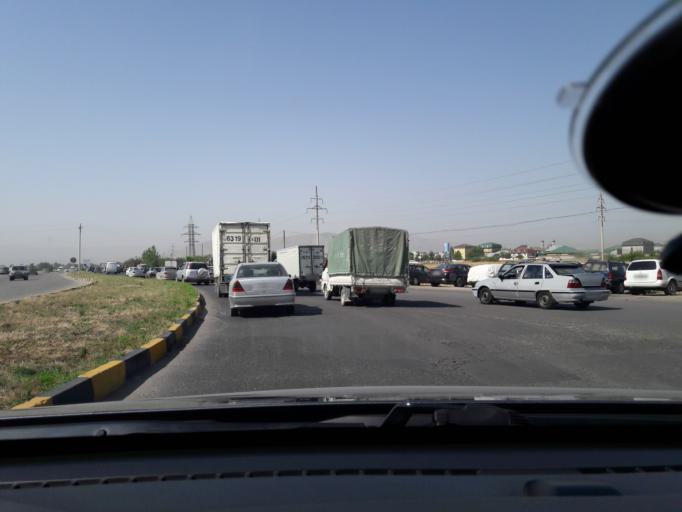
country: TJ
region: Dushanbe
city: Dushanbe
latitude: 38.5002
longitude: 68.7558
